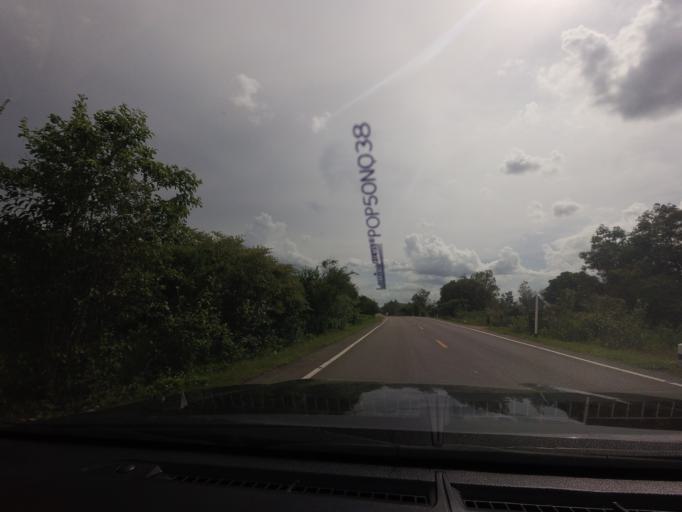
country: TH
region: Kanchanaburi
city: Bo Phloi
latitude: 14.1660
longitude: 99.4334
